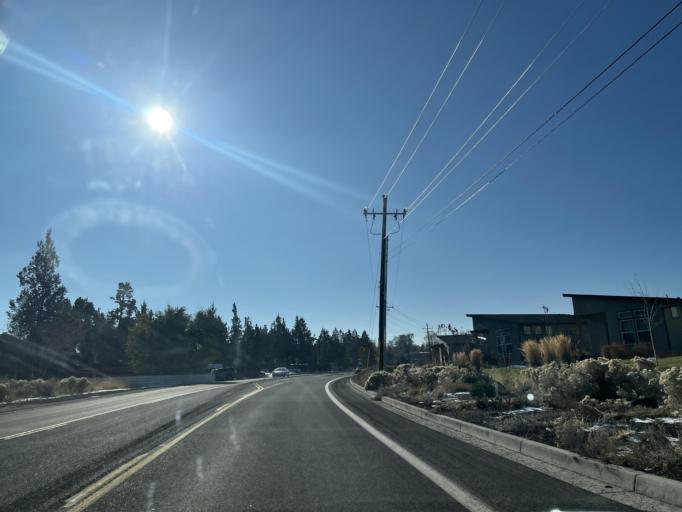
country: US
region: Oregon
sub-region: Deschutes County
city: Bend
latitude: 44.0797
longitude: -121.2825
